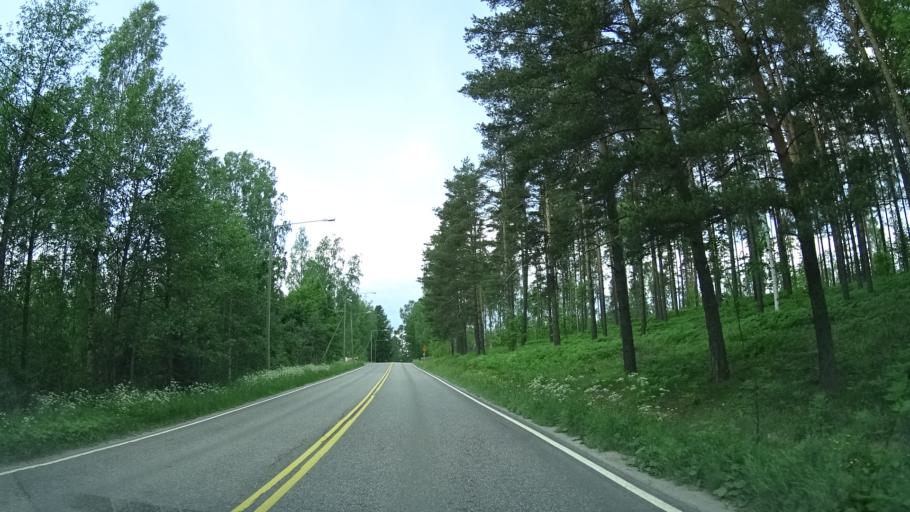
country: FI
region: Uusimaa
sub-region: Helsinki
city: Kirkkonummi
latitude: 60.2068
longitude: 24.4928
